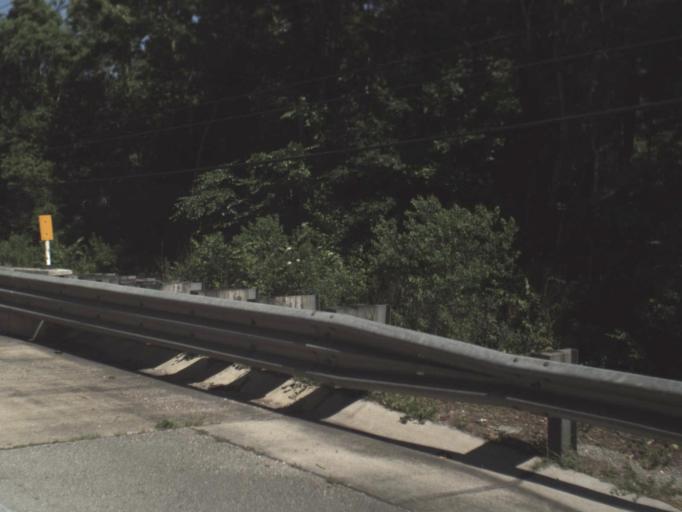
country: US
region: Florida
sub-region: Duval County
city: Baldwin
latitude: 30.3135
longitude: -81.8559
